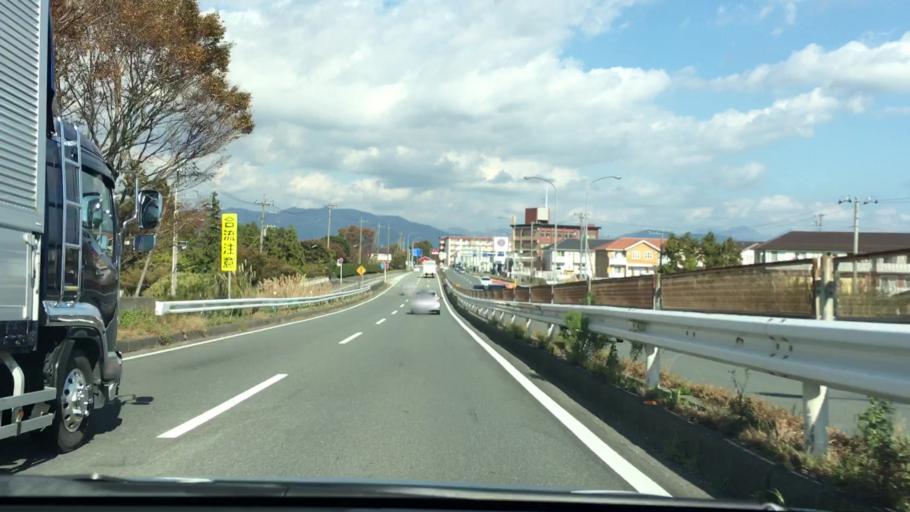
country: JP
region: Shizuoka
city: Gotemba
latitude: 35.3135
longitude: 138.9280
